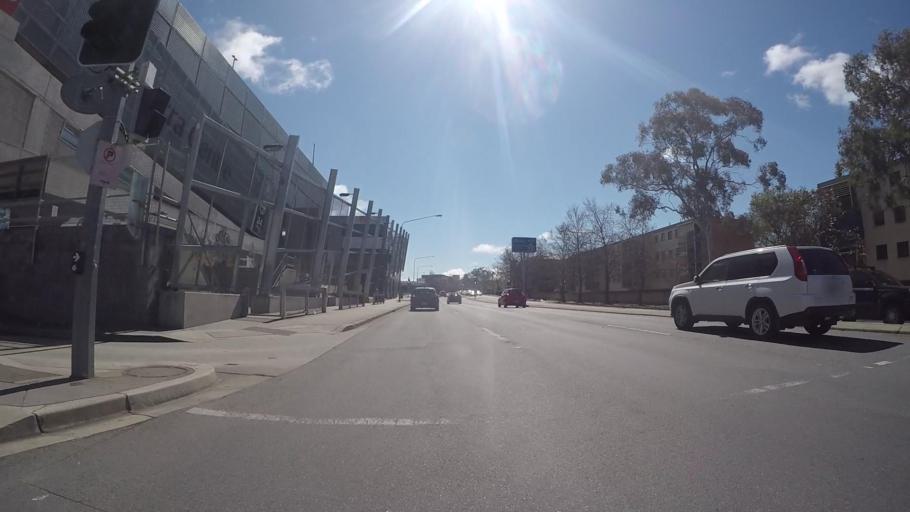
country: AU
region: Australian Capital Territory
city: Canberra
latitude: -35.2782
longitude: 149.1348
